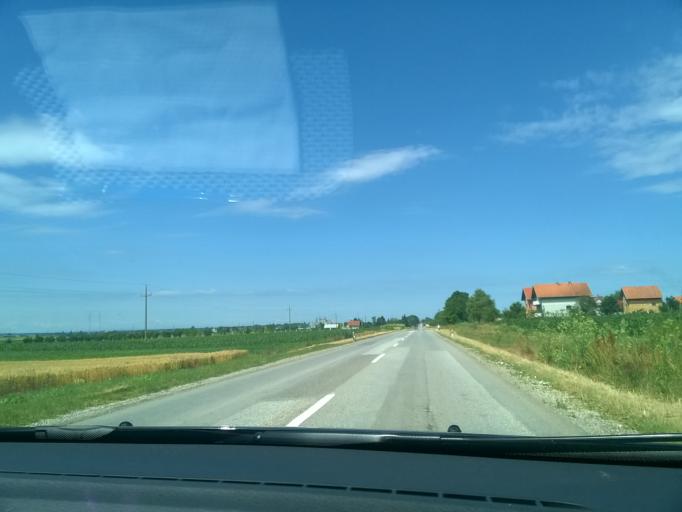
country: RS
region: Autonomna Pokrajina Vojvodina
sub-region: Sremski Okrug
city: Ruma
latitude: 45.0092
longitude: 19.8630
